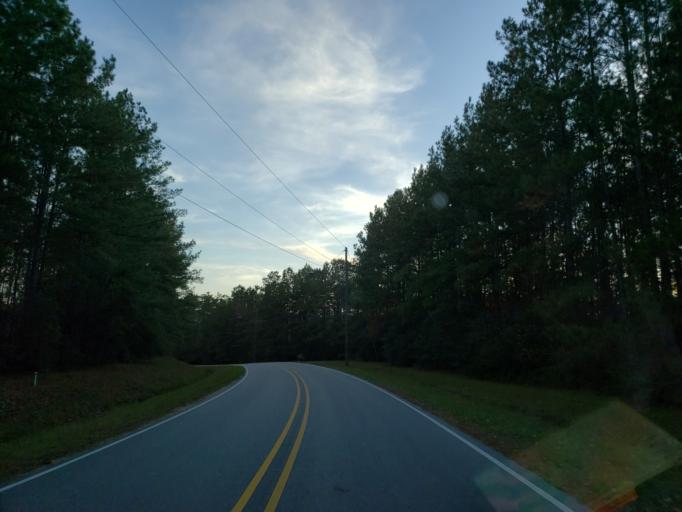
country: US
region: Mississippi
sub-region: Forrest County
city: Hattiesburg
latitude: 31.2726
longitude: -89.3095
